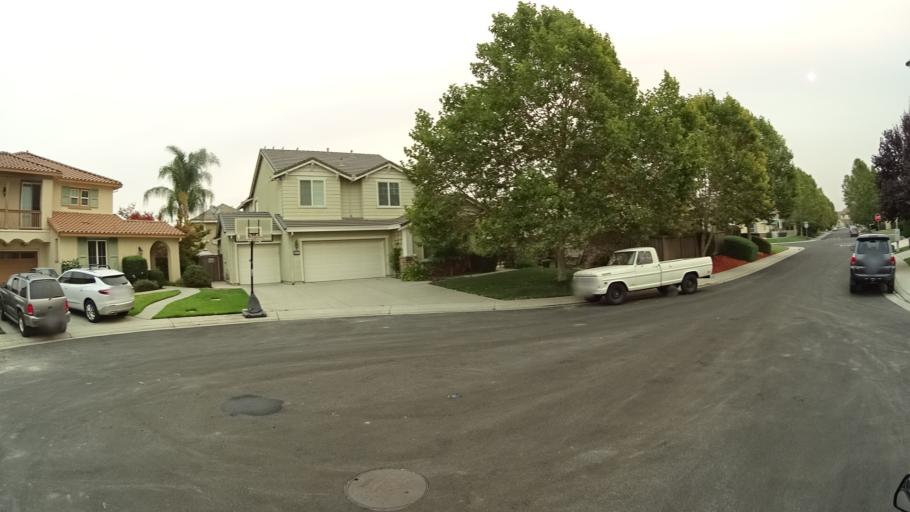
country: US
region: California
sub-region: Sacramento County
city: Laguna
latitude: 38.3797
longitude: -121.4437
